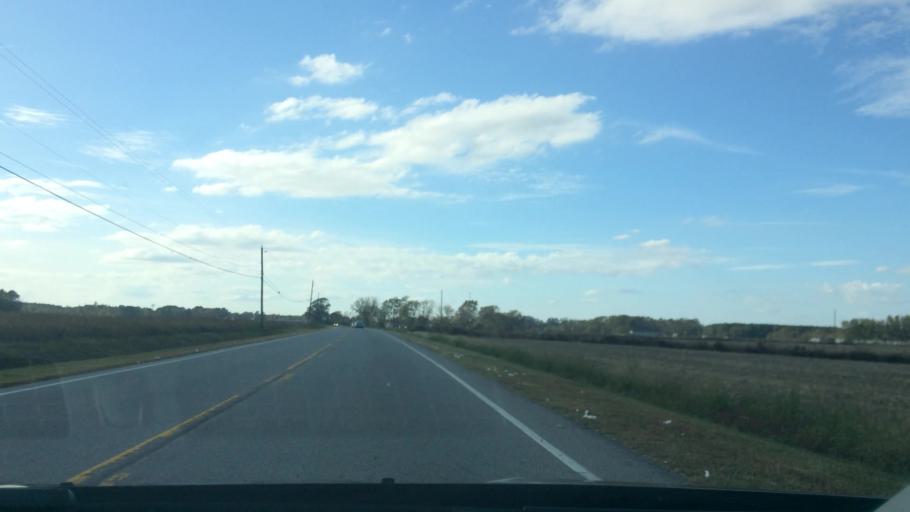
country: US
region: North Carolina
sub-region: Greene County
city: Snow Hill
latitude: 35.4376
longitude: -77.7747
